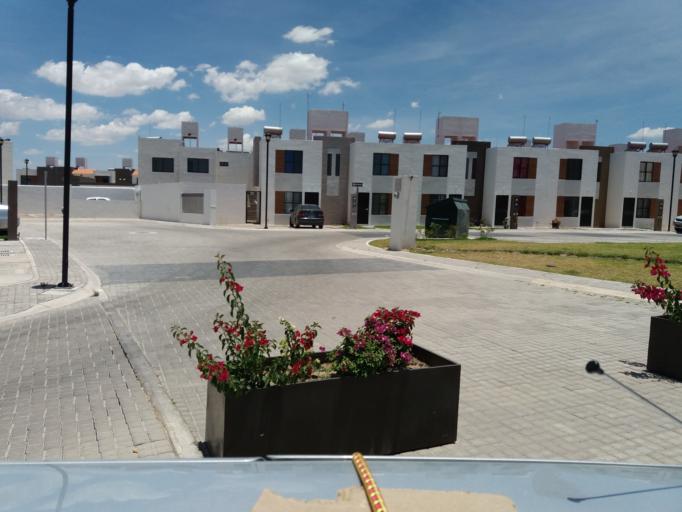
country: MX
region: Aguascalientes
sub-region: Aguascalientes
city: San Sebastian [Fraccionamiento]
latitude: 21.8034
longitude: -102.3026
